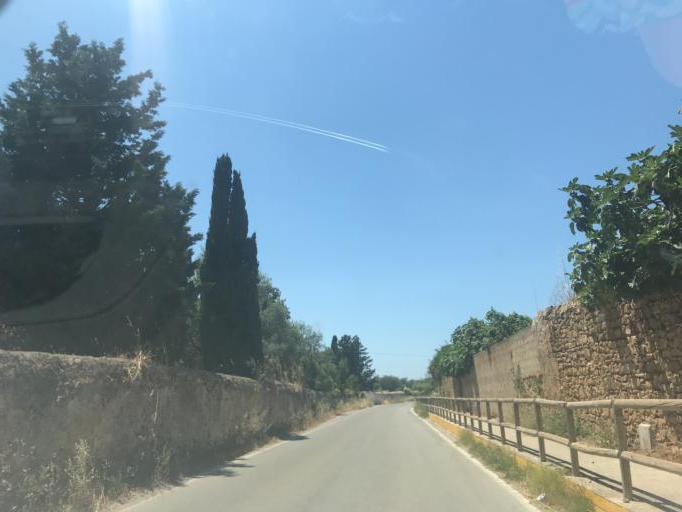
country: IT
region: Sardinia
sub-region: Provincia di Sassari
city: Alghero
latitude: 40.5504
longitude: 8.3465
